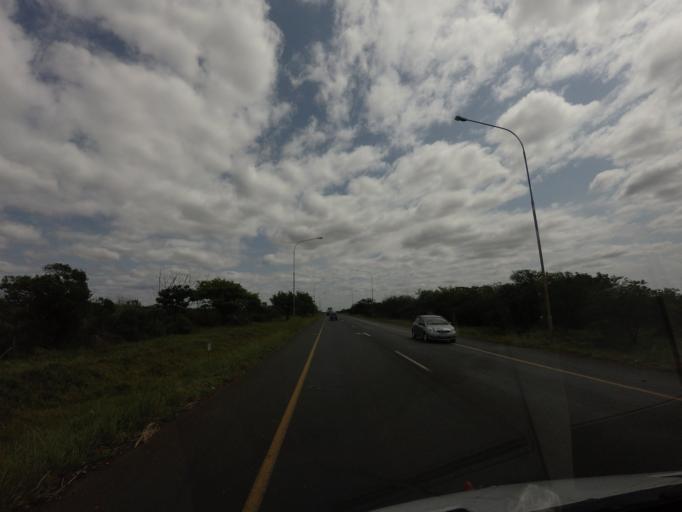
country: ZA
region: KwaZulu-Natal
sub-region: uMkhanyakude District Municipality
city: Hluhluwe
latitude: -28.0938
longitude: 32.2688
